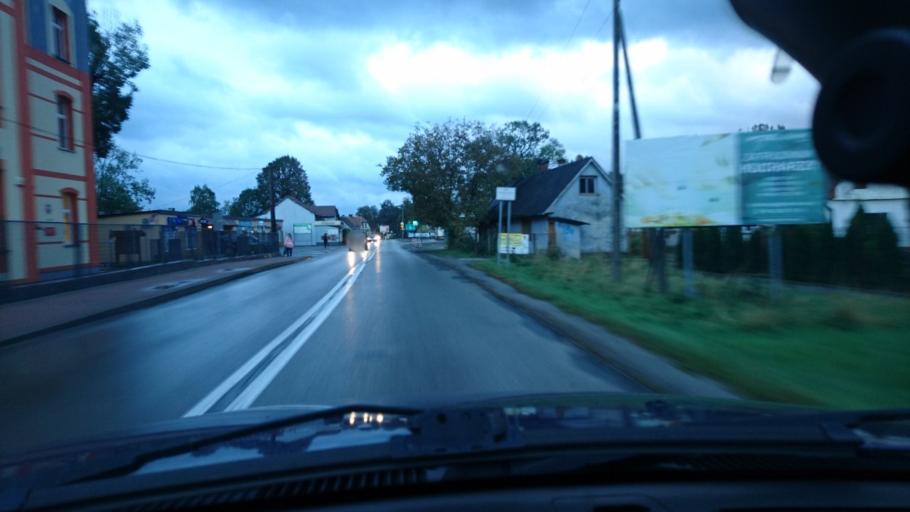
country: PL
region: Silesian Voivodeship
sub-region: Powiat bielski
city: Buczkowice
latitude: 49.7303
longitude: 19.0684
